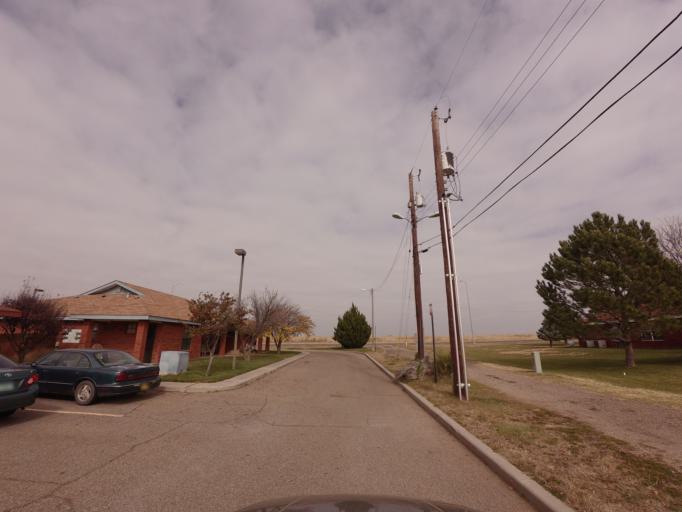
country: US
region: New Mexico
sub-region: Curry County
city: Clovis
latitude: 34.4334
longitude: -103.2253
